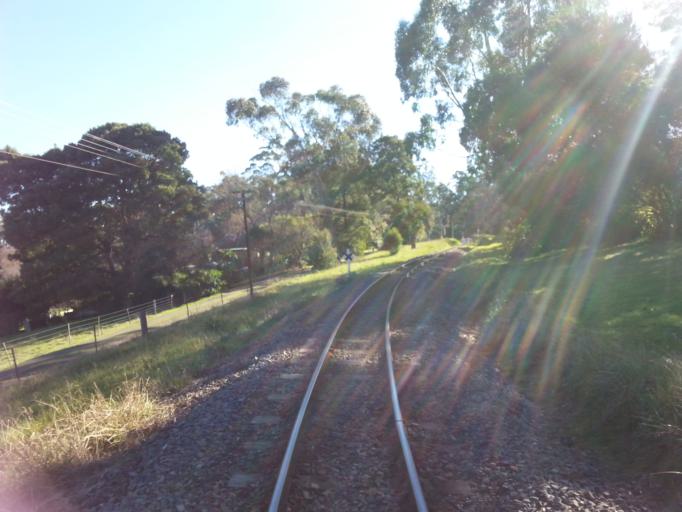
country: AU
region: Victoria
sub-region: Yarra Ranges
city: Selby
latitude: -37.9222
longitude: 145.4074
